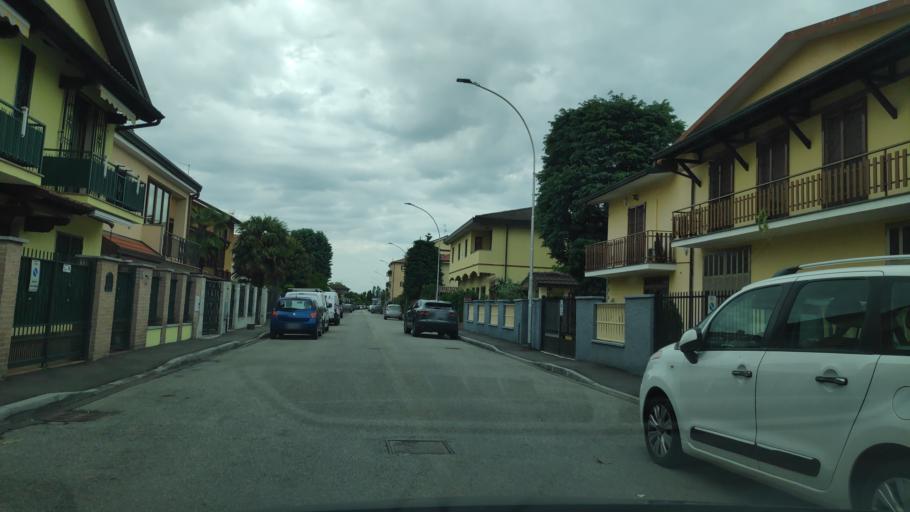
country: IT
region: Lombardy
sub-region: Citta metropolitana di Milano
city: Caleppio
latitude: 45.4360
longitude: 9.3838
